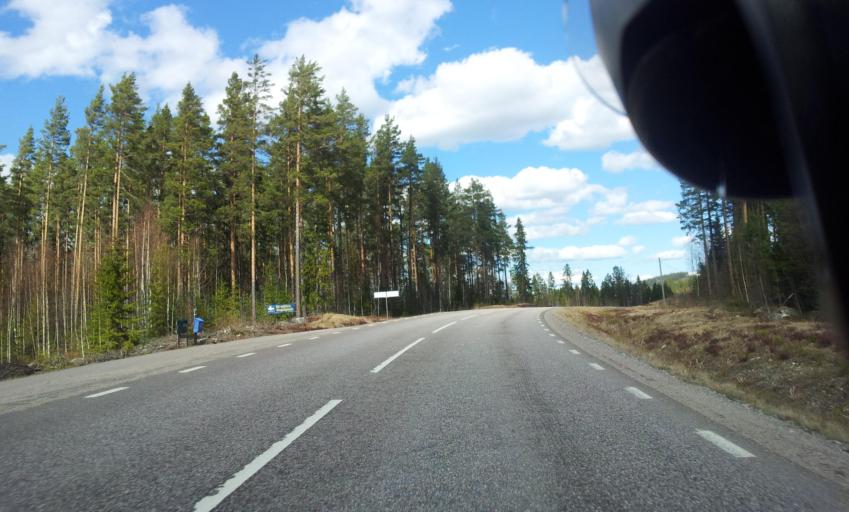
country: SE
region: Gaevleborg
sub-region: Ovanakers Kommun
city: Edsbyn
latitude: 61.2103
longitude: 15.8708
